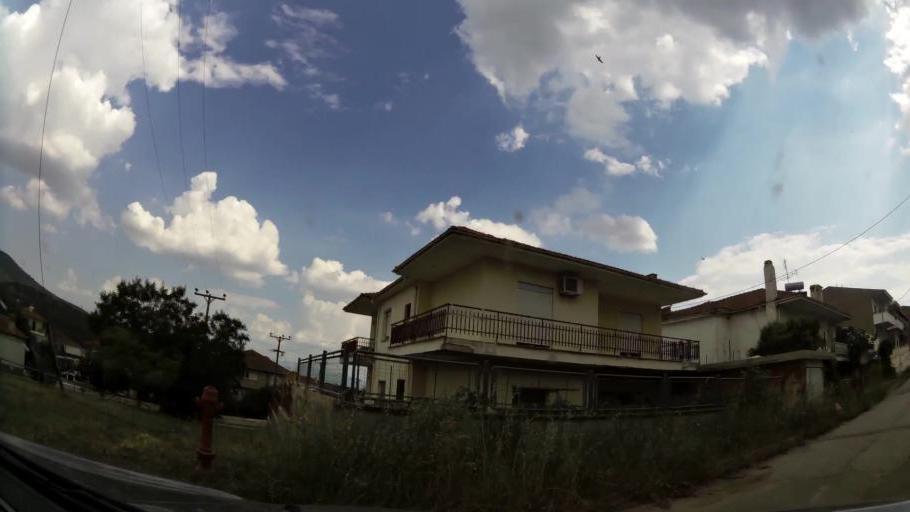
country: GR
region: West Macedonia
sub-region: Nomos Kozanis
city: Koila
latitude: 40.3272
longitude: 21.8235
